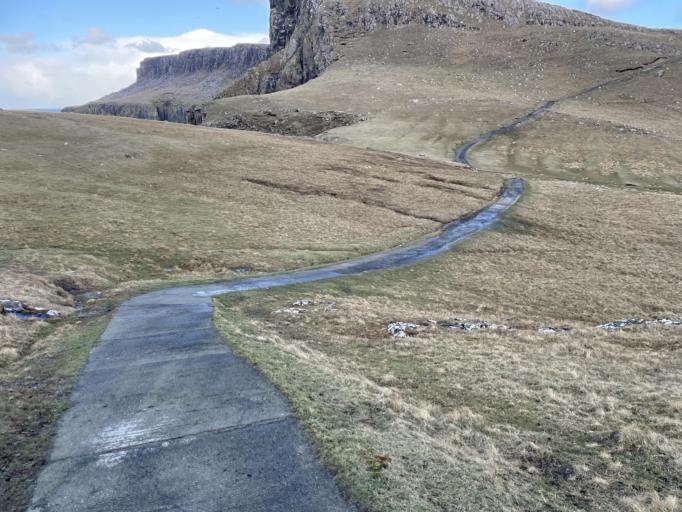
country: GB
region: Scotland
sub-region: Eilean Siar
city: Harris
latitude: 57.4243
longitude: -6.7861
